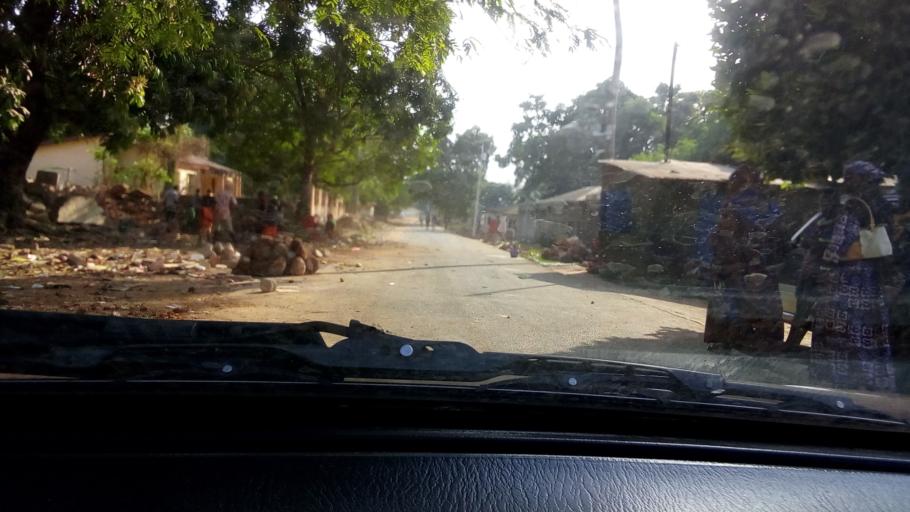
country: GN
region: Kindia
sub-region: Prefecture de Dubreka
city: Dubreka
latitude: 9.7922
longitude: -13.5254
